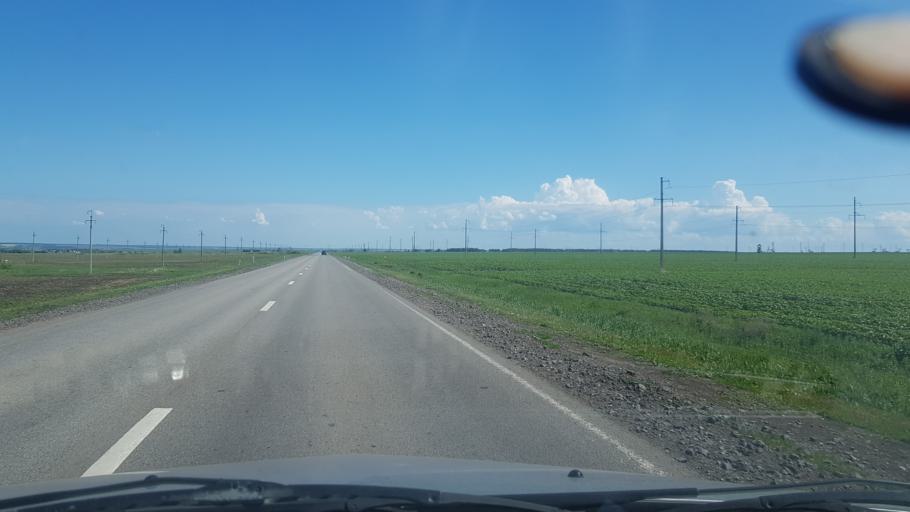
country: RU
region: Tatarstan
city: Nurlat
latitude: 54.4624
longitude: 50.8331
